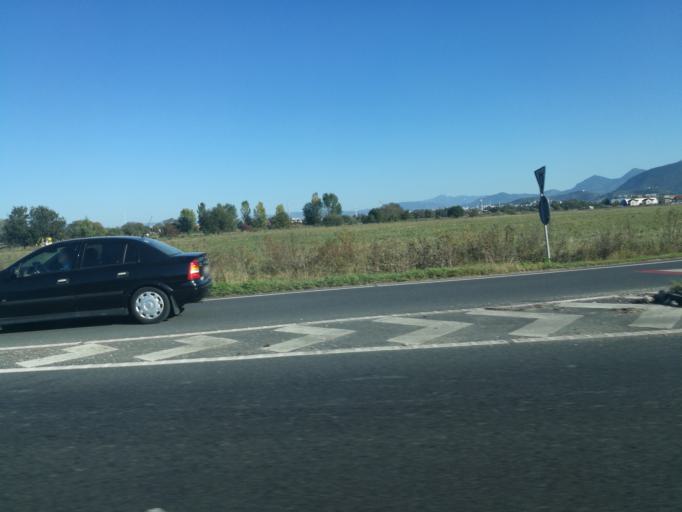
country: RO
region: Brasov
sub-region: Comuna Ghimbav
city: Ghimbav
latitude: 45.6795
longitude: 25.5560
